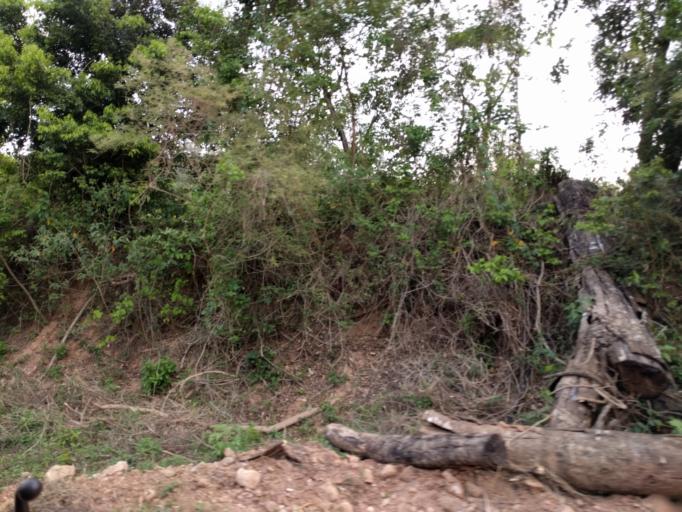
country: BO
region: Santa Cruz
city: Santa Rita
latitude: -17.9321
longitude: -63.3761
